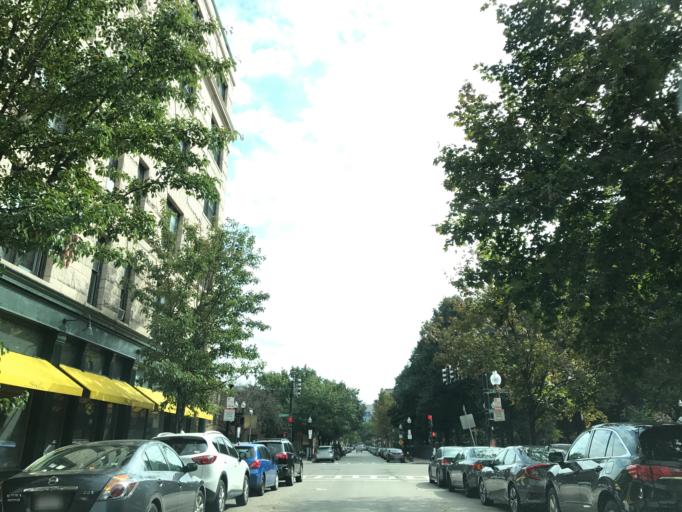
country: US
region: Massachusetts
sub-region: Suffolk County
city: Boston
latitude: 42.3400
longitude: -71.0729
